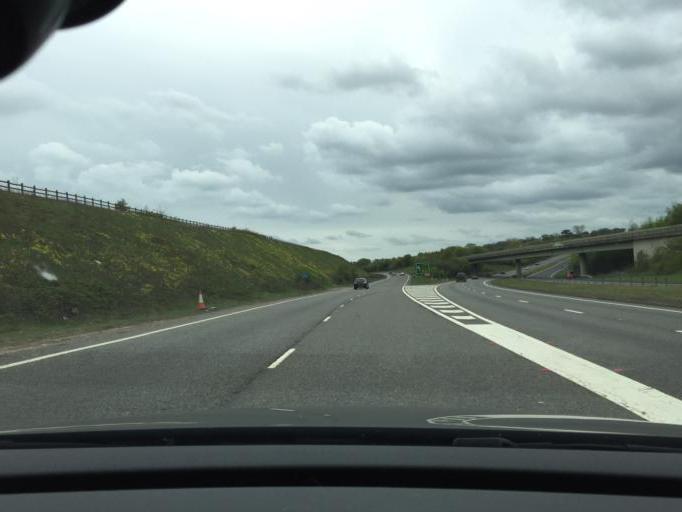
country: GB
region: England
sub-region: West Berkshire
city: Winterbourne
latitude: 51.4366
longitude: -1.3211
